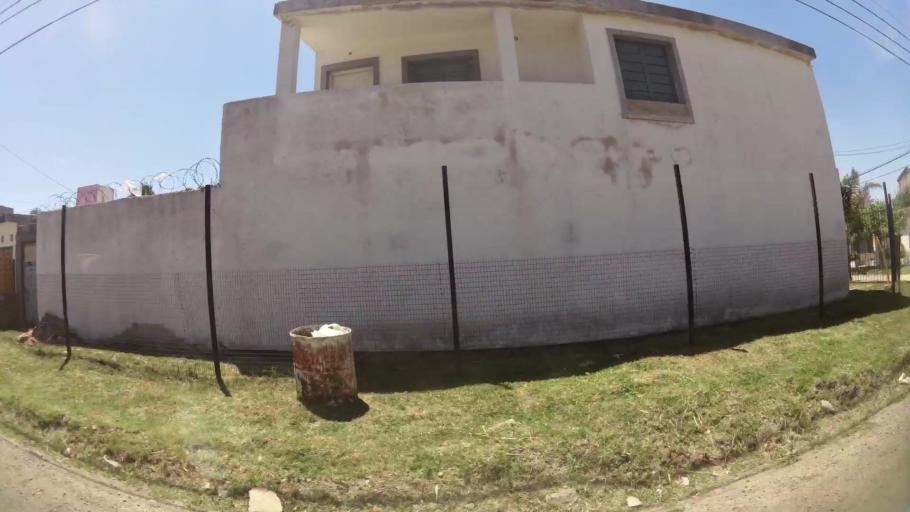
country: AR
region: Cordoba
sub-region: Departamento de Capital
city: Cordoba
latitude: -31.3864
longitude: -64.1414
